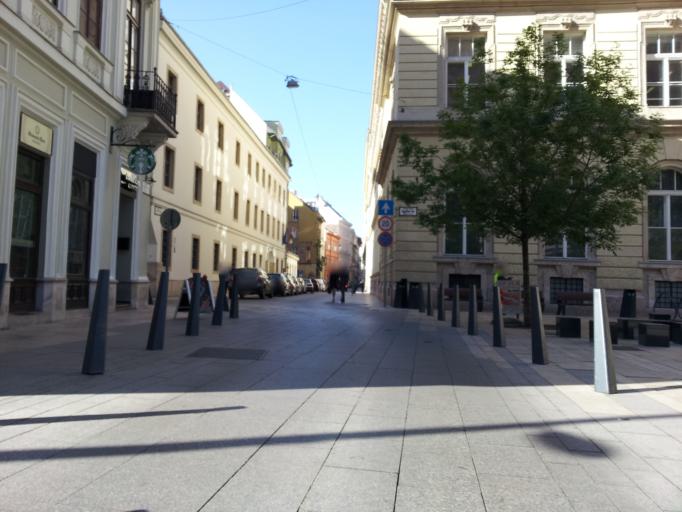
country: HU
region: Budapest
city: Budapest IX. keruelet
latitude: 47.4909
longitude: 19.0587
